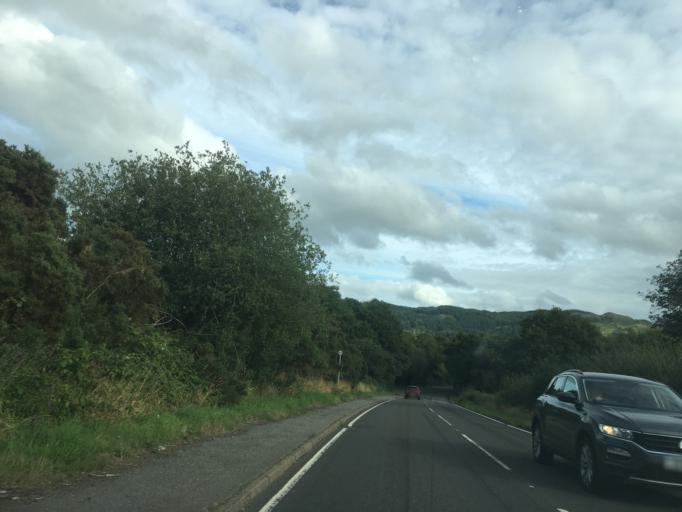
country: GB
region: Scotland
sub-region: Argyll and Bute
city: Oban
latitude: 56.3751
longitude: -5.4423
